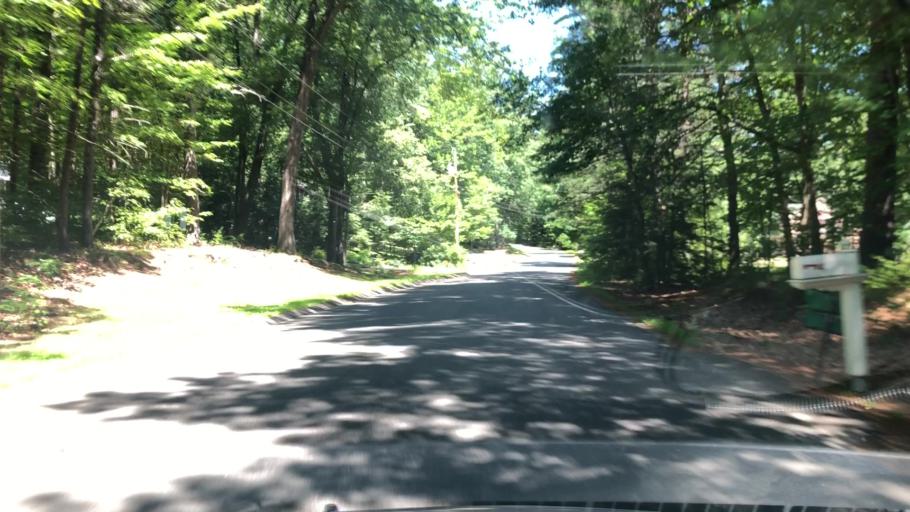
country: US
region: New Hampshire
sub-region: Hillsborough County
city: Milford
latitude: 42.8363
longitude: -71.5765
